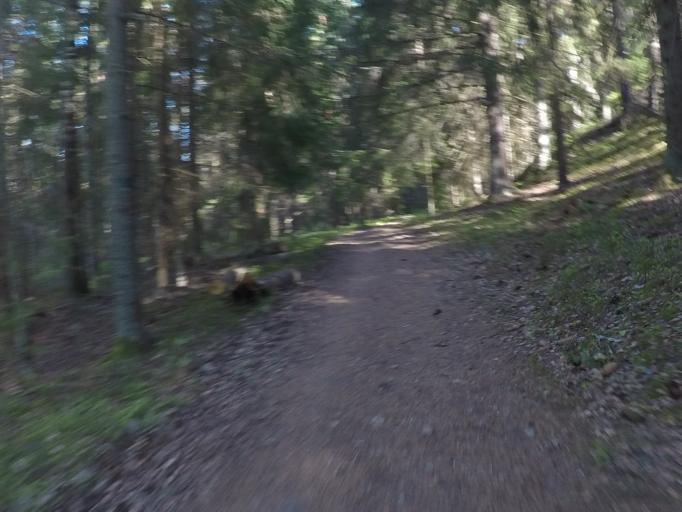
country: SE
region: Soedermanland
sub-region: Eskilstuna Kommun
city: Eskilstuna
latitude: 59.4047
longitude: 16.5358
